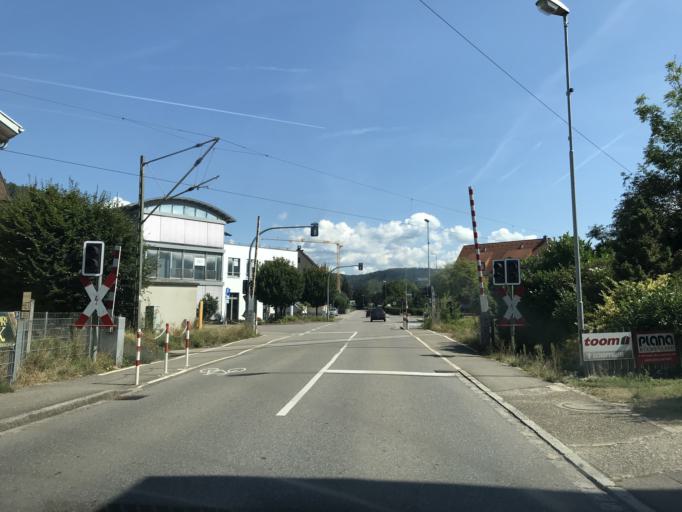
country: DE
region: Baden-Wuerttemberg
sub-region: Freiburg Region
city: Maulburg
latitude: 47.6443
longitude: 7.7825
